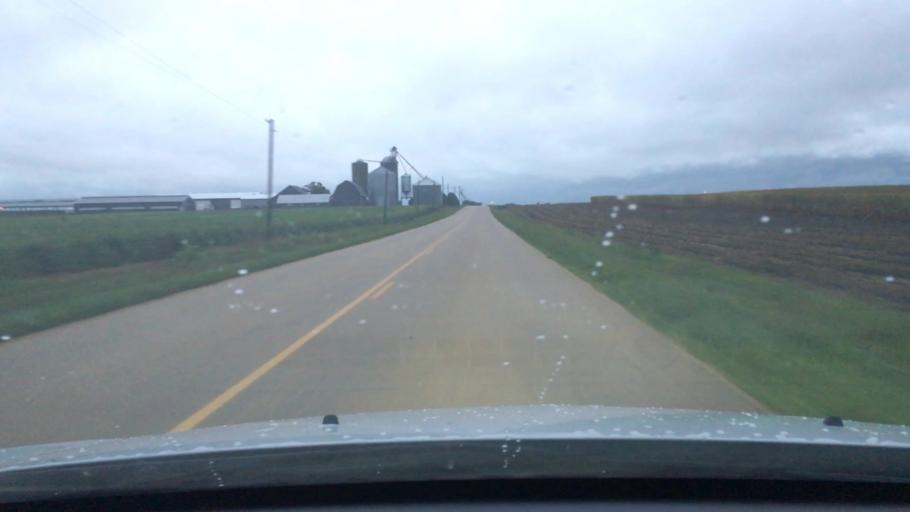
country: US
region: Illinois
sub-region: DeKalb County
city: Malta
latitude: 41.8549
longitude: -88.9613
